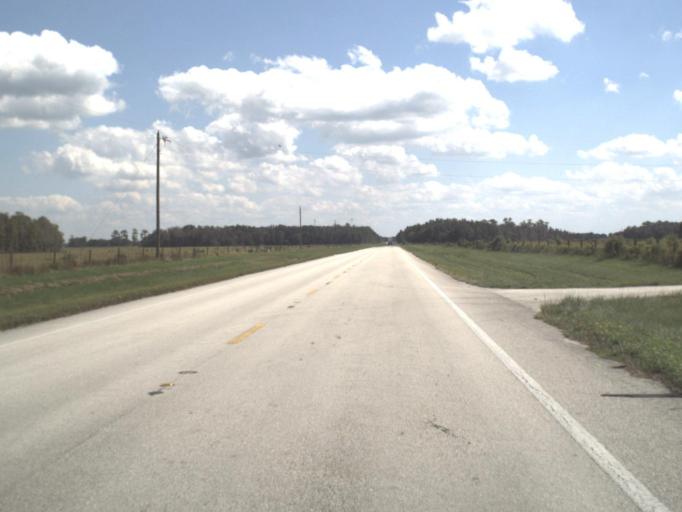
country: US
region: Florida
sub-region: Highlands County
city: Sebring
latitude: 27.4410
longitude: -81.6132
